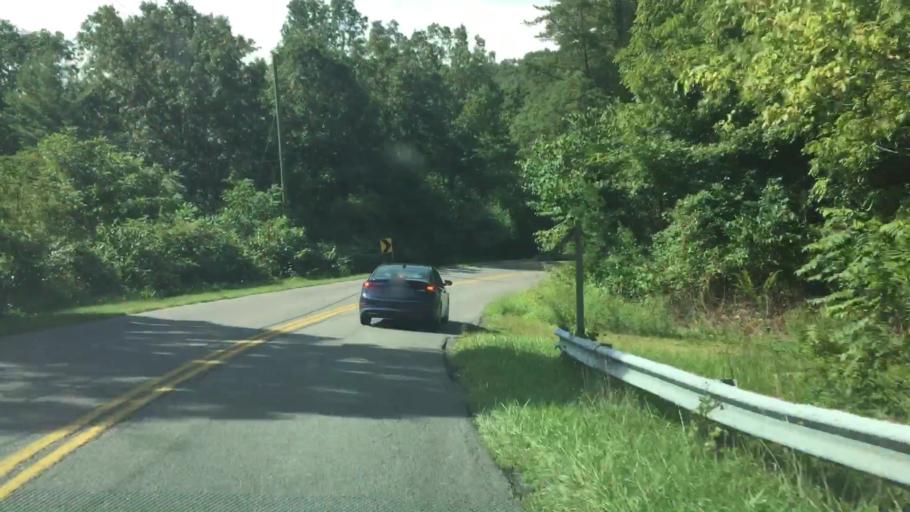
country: US
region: Tennessee
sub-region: Sullivan County
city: Fairmount
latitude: 36.6048
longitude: -82.0739
